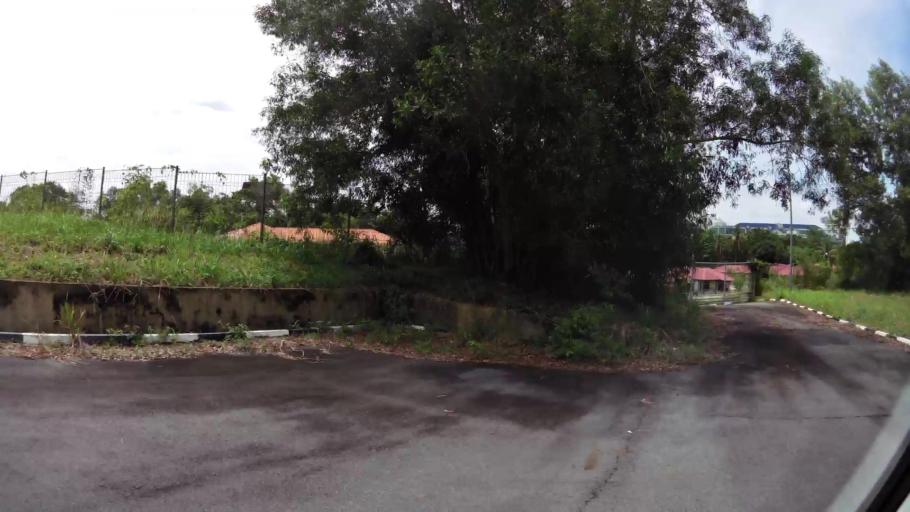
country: BN
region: Brunei and Muara
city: Bandar Seri Begawan
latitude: 4.9034
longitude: 114.9132
